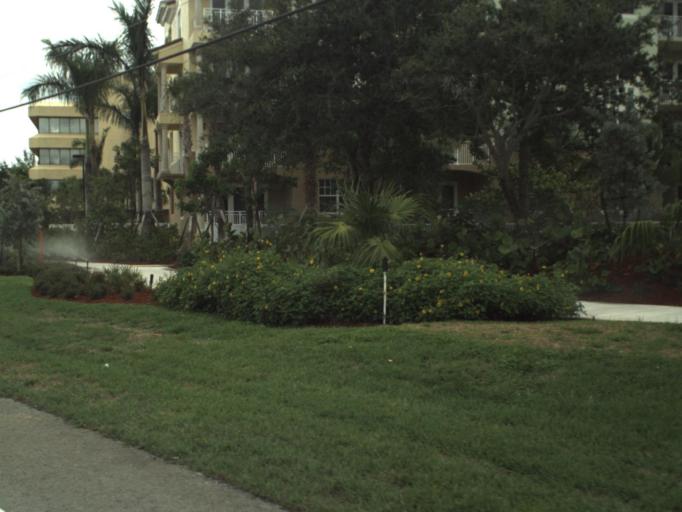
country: US
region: Florida
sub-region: Palm Beach County
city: Jupiter
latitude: 26.9236
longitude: -80.0756
